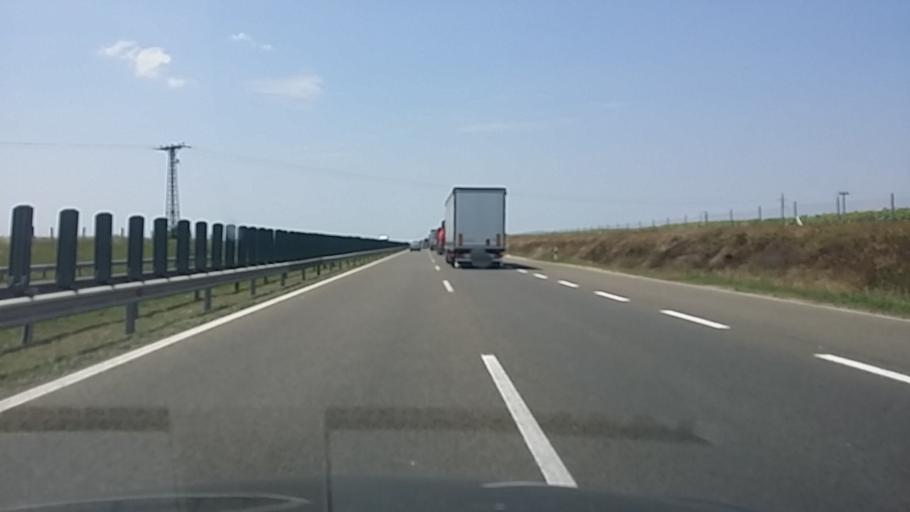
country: HU
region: Gyor-Moson-Sopron
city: Toltestava
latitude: 47.6615
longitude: 17.7459
